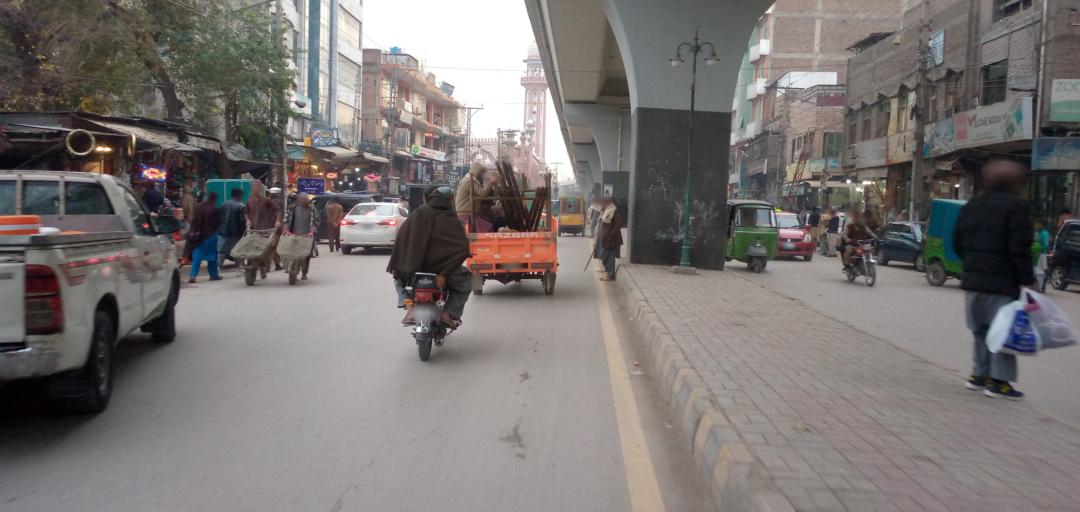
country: PK
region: Khyber Pakhtunkhwa
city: Peshawar
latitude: 33.9969
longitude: 71.5412
